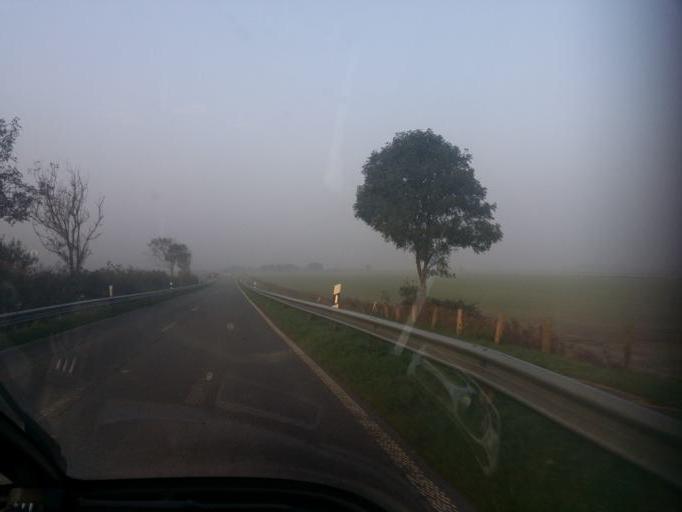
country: DE
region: Schleswig-Holstein
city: Wobbenbull
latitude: 54.5137
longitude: 8.9450
